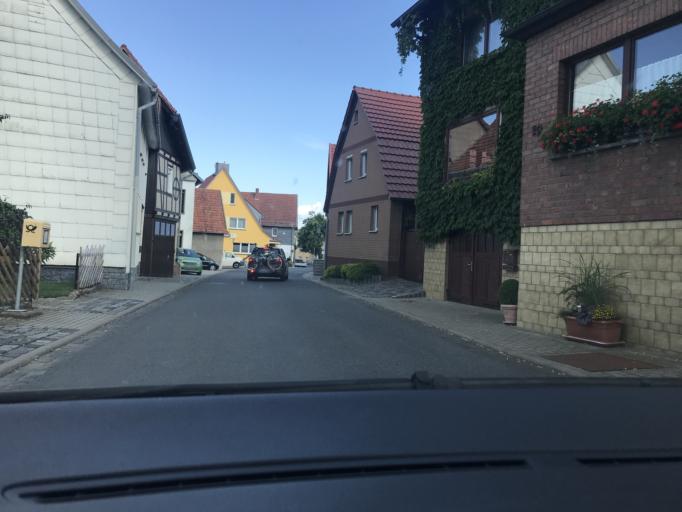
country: DE
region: Thuringia
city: Kefferhausen
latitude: 51.3135
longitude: 10.2831
